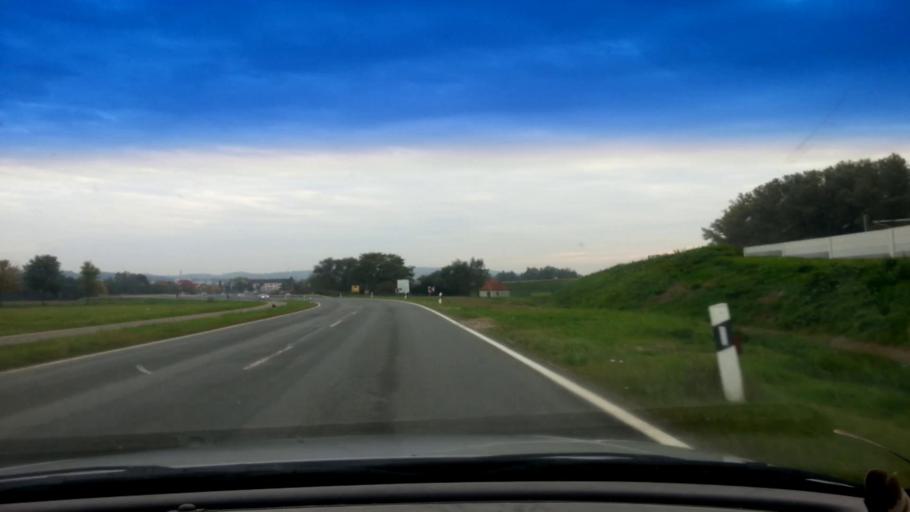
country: DE
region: Bavaria
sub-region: Upper Franconia
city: Zapfendorf
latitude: 50.0262
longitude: 10.9384
